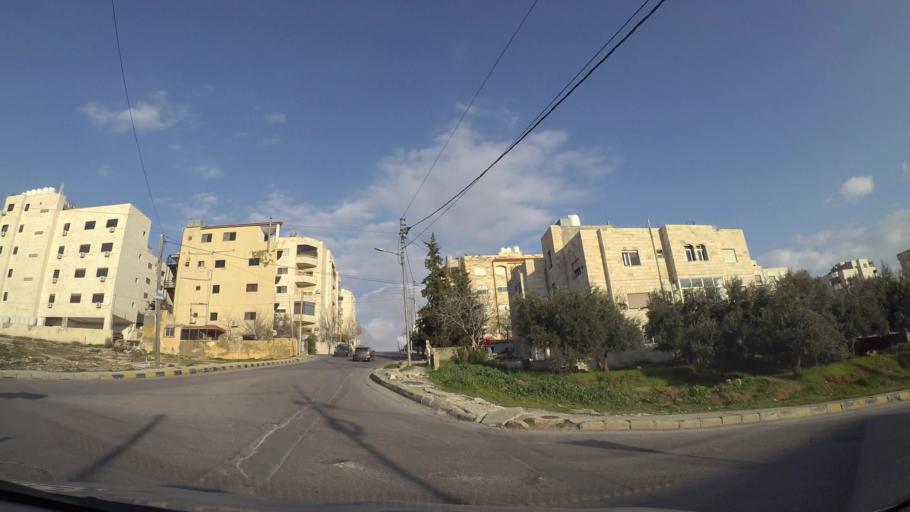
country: JO
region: Amman
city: Al Jubayhah
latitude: 31.9946
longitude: 35.8663
